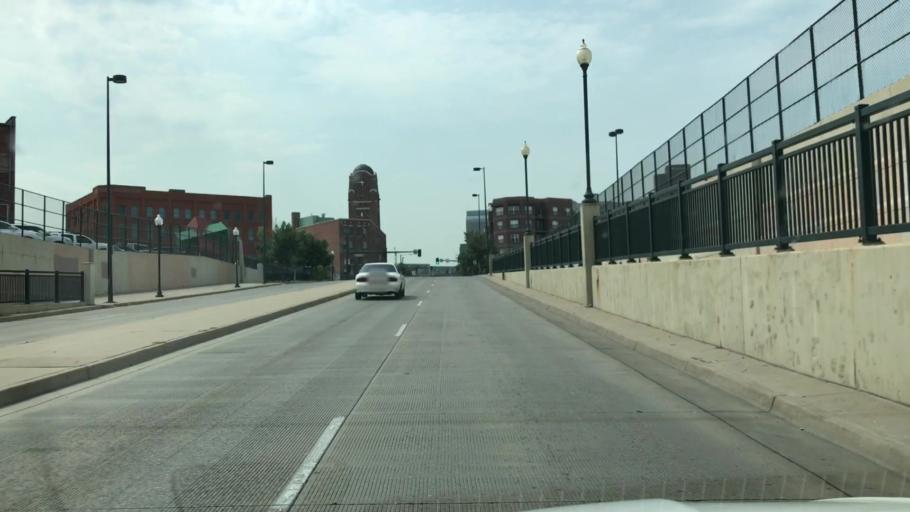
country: US
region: Colorado
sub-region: Denver County
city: Denver
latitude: 39.7609
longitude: -104.9880
